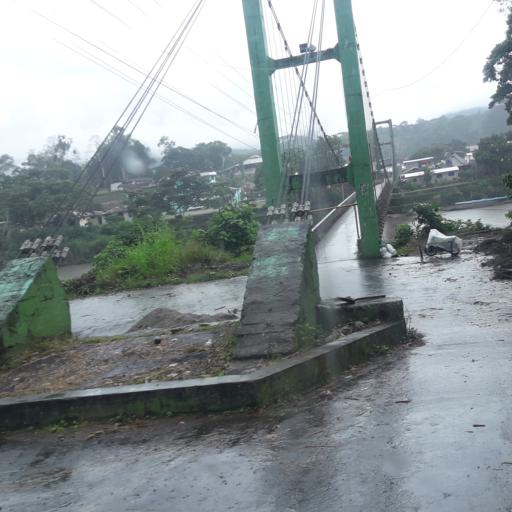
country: EC
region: Napo
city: Tena
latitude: -1.0378
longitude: -77.6669
